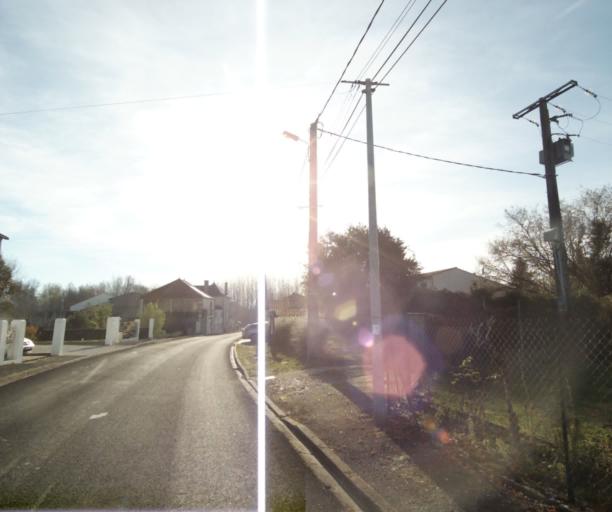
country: FR
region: Poitou-Charentes
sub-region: Departement de la Charente-Maritime
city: Chaniers
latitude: 45.7094
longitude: -0.5277
